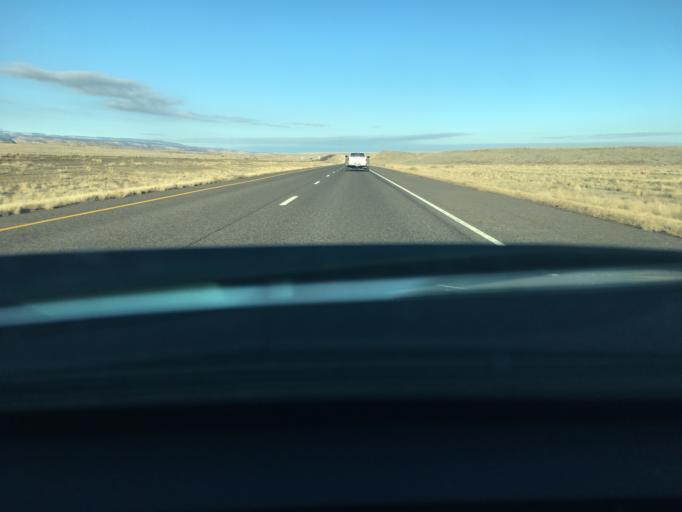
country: US
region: Colorado
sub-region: Delta County
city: Delta
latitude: 38.7953
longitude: -108.2613
